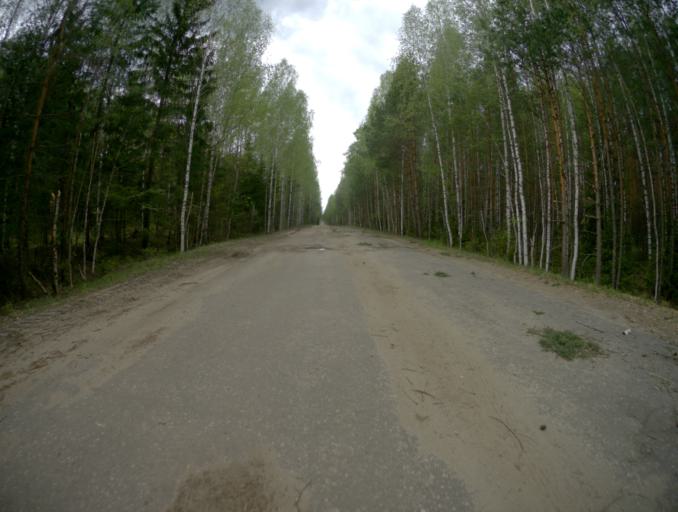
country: RU
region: Vladimir
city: Velikodvorskiy
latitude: 55.2441
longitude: 40.7237
